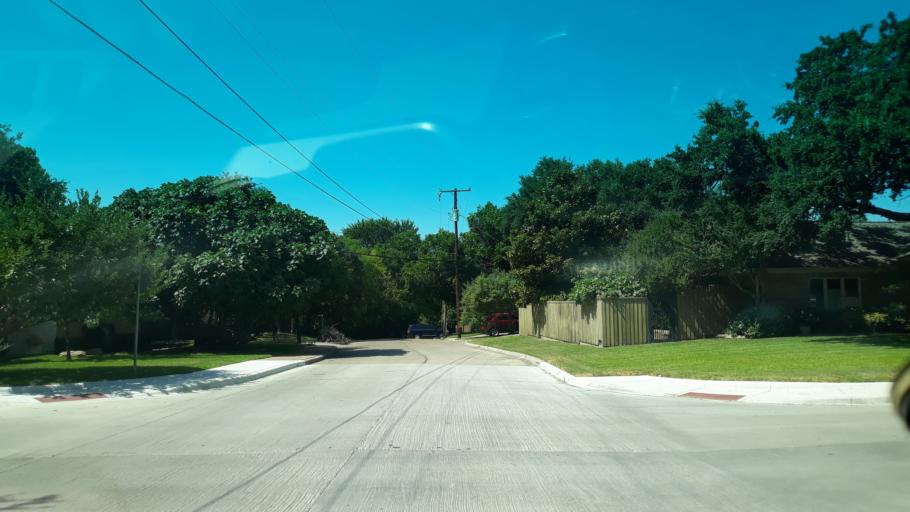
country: US
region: Texas
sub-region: Dallas County
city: Highland Park
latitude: 32.8212
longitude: -96.7465
